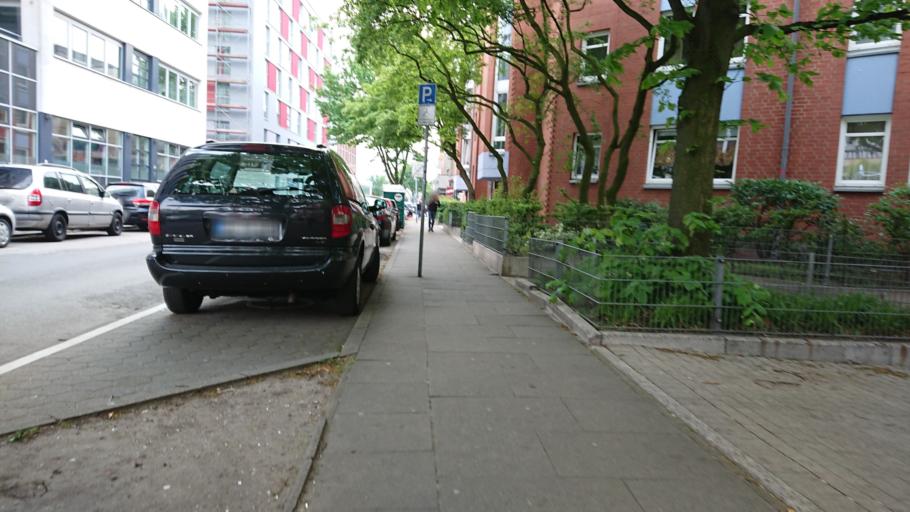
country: DE
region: Hamburg
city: St. Georg
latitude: 53.5562
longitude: 10.0164
